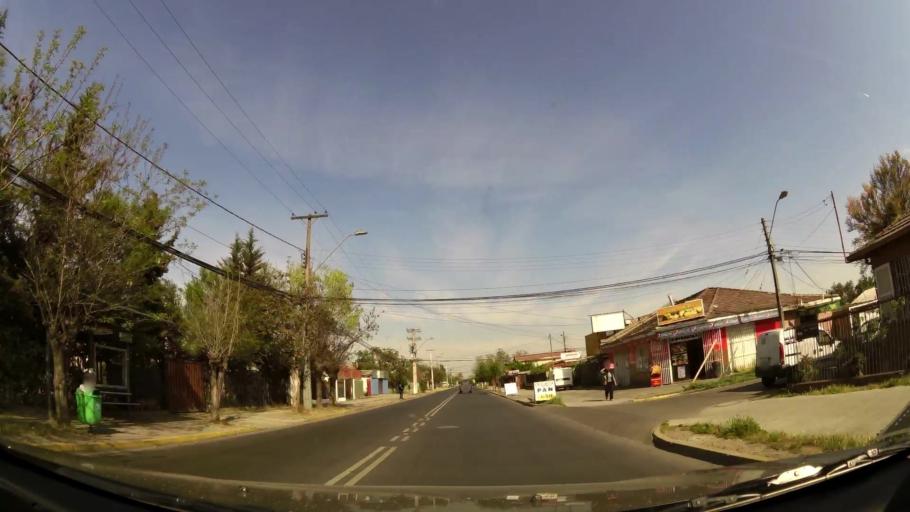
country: CL
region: Santiago Metropolitan
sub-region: Provincia de Cordillera
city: Puente Alto
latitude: -33.5628
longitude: -70.5792
